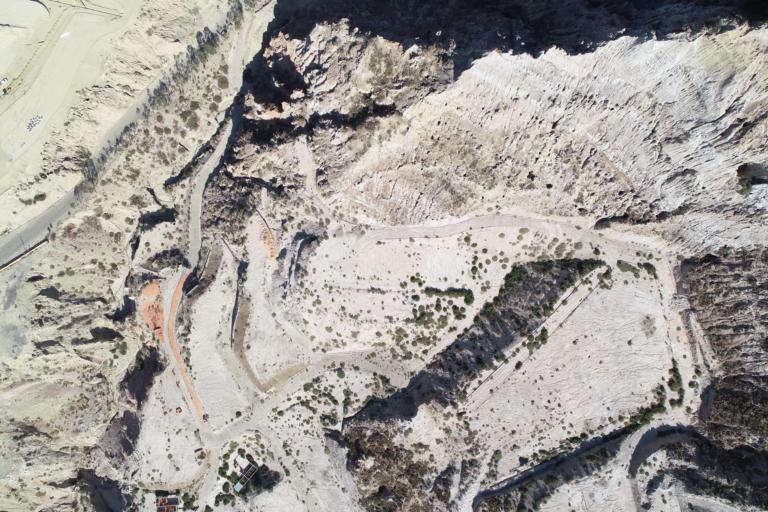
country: BO
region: La Paz
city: La Paz
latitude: -16.5555
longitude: -68.1084
